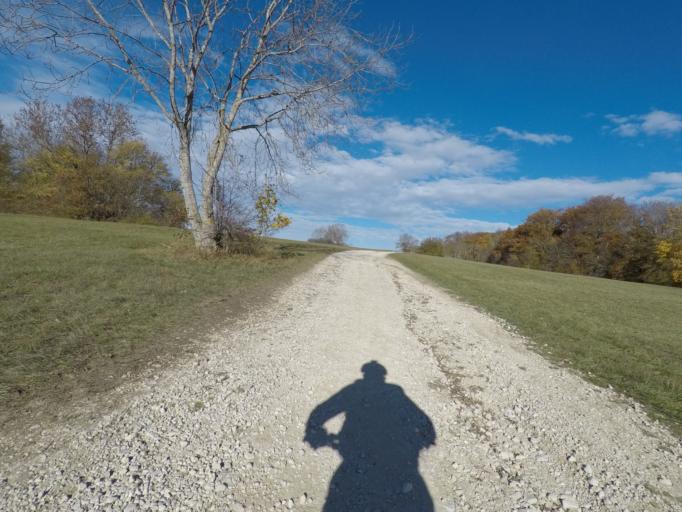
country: DE
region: Baden-Wuerttemberg
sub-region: Tuebingen Region
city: Pfullingen
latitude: 48.4124
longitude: 9.2435
